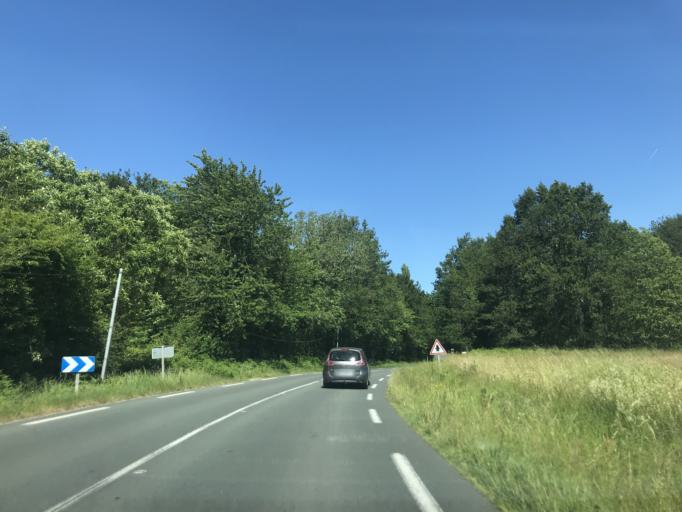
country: FR
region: Poitou-Charentes
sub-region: Departement de la Charente-Maritime
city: Cozes
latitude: 45.5719
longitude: -0.7592
